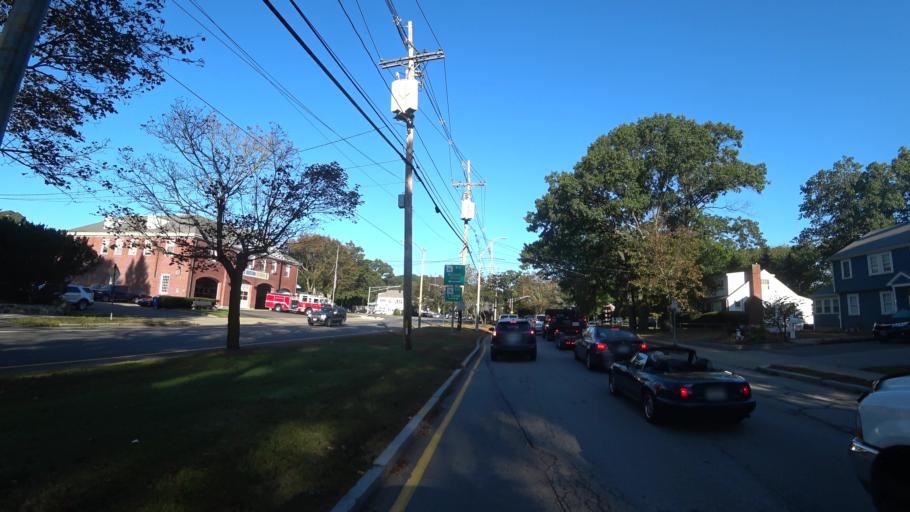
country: US
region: Massachusetts
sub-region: Middlesex County
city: Newton
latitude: 42.3406
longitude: -71.2378
